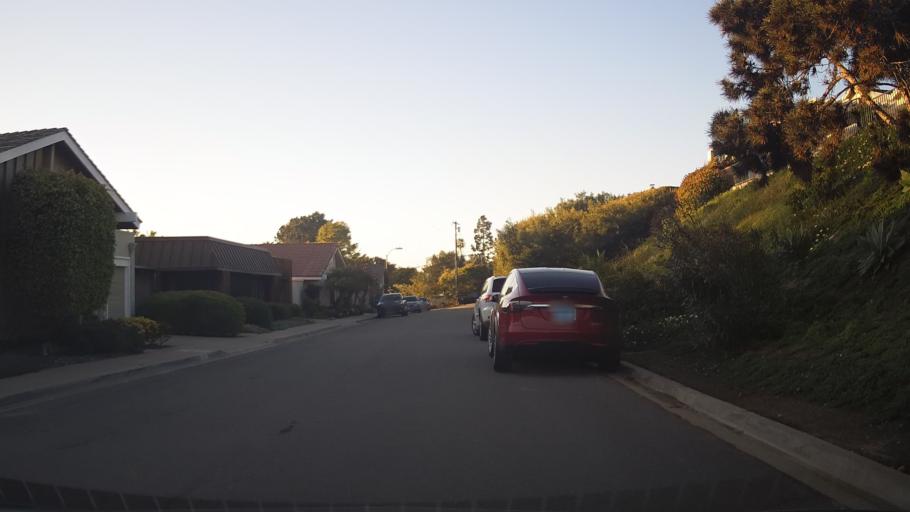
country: US
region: California
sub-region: San Diego County
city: Del Mar
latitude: 32.9519
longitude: -117.2596
